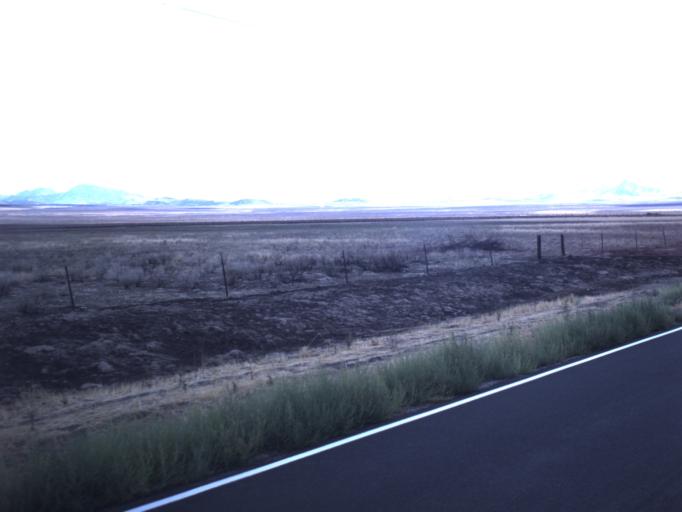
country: US
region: Utah
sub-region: Tooele County
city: Grantsville
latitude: 40.2980
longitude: -112.6516
